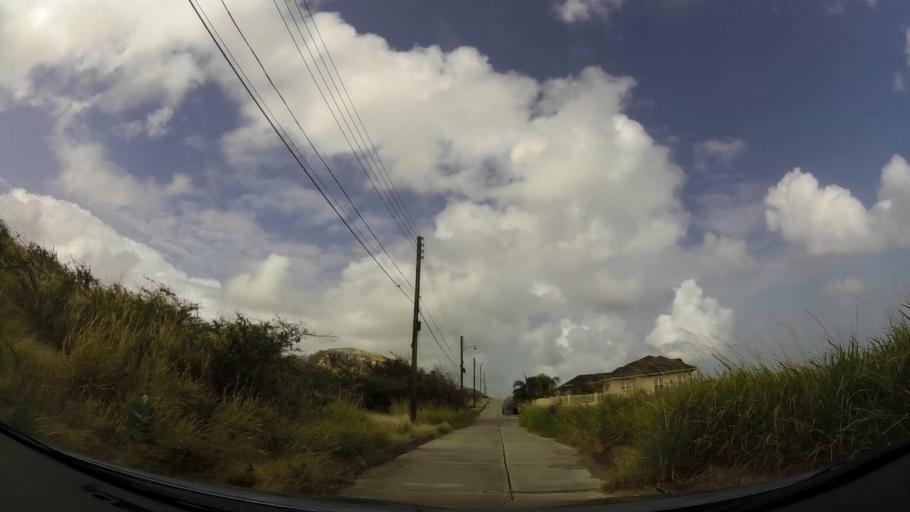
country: KN
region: Saint Peter Basseterre
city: Monkey Hill
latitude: 17.3044
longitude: -62.6958
